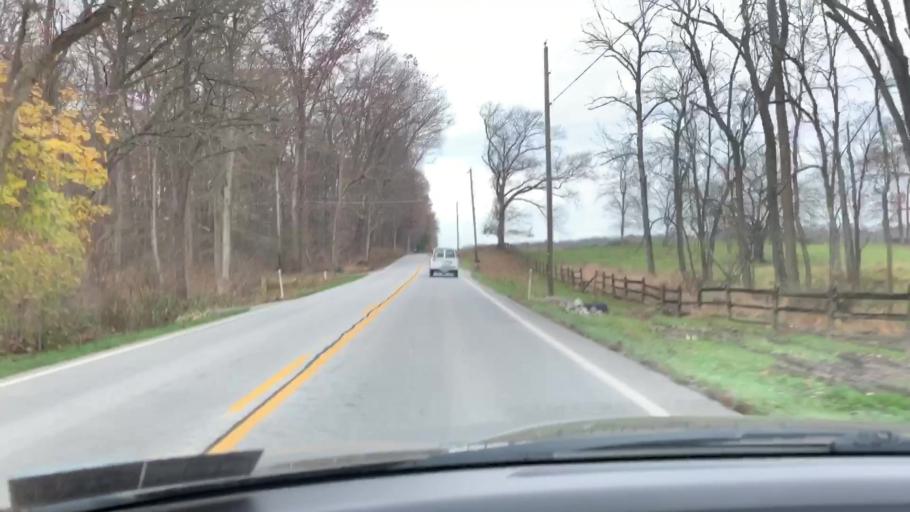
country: US
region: Pennsylvania
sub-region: Adams County
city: Lake Meade
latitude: 39.9427
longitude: -77.0767
